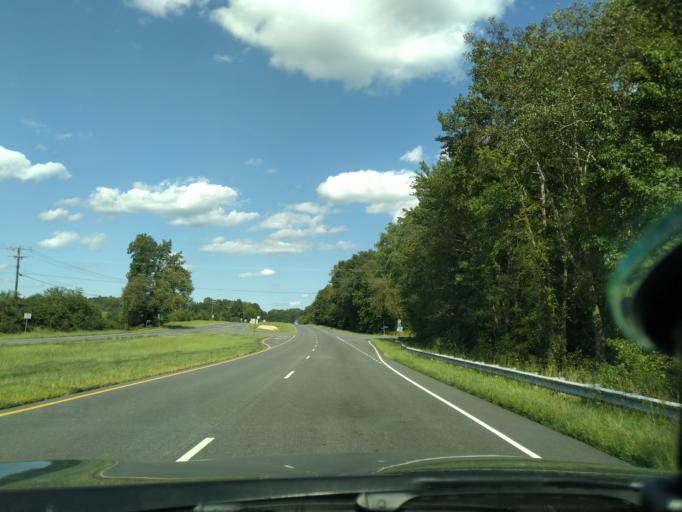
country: US
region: Virginia
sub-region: Caroline County
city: Bowling Green
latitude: 38.0343
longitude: -77.3716
